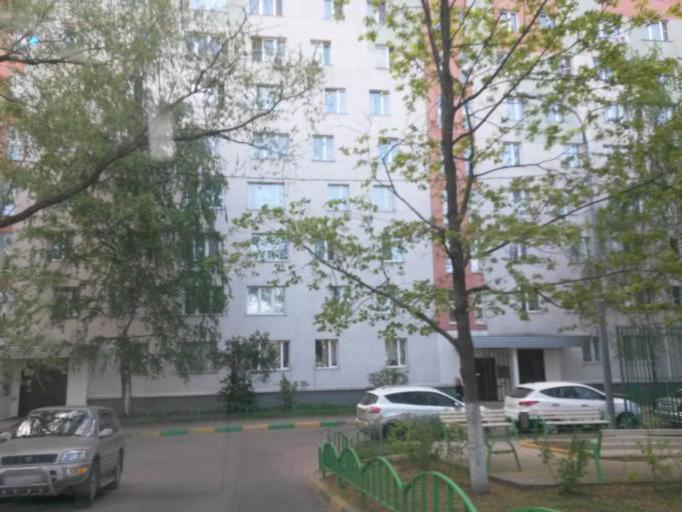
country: RU
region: Moscow
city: Mar'ino
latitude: 55.6538
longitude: 37.7115
